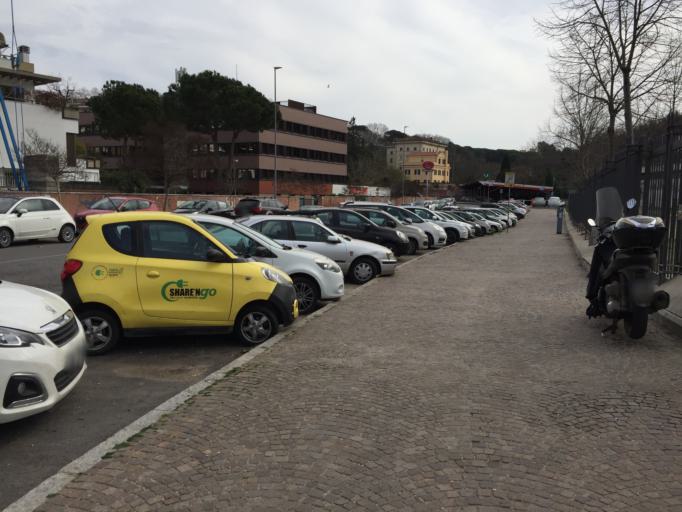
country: VA
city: Vatican City
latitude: 41.8955
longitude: 12.4559
